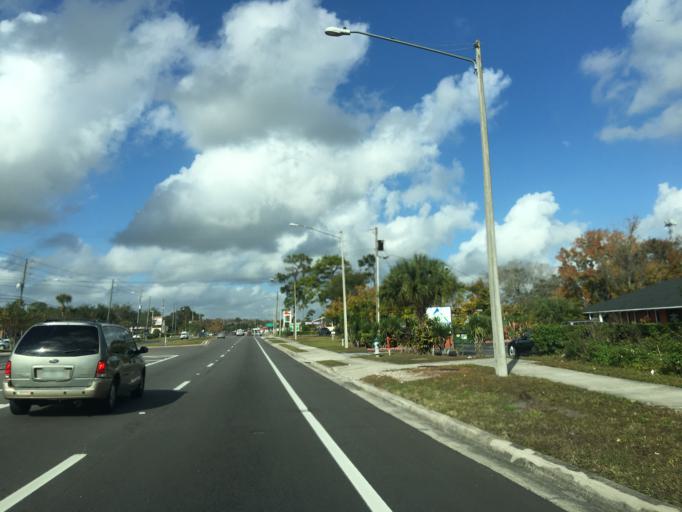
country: US
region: Florida
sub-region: Orange County
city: Azalea Park
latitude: 28.5142
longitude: -81.2871
